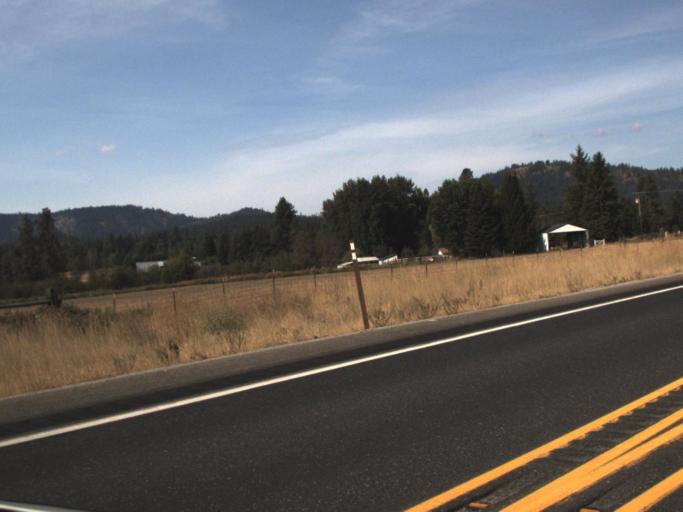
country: US
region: Washington
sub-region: Spokane County
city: Deer Park
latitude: 47.9961
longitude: -117.5715
